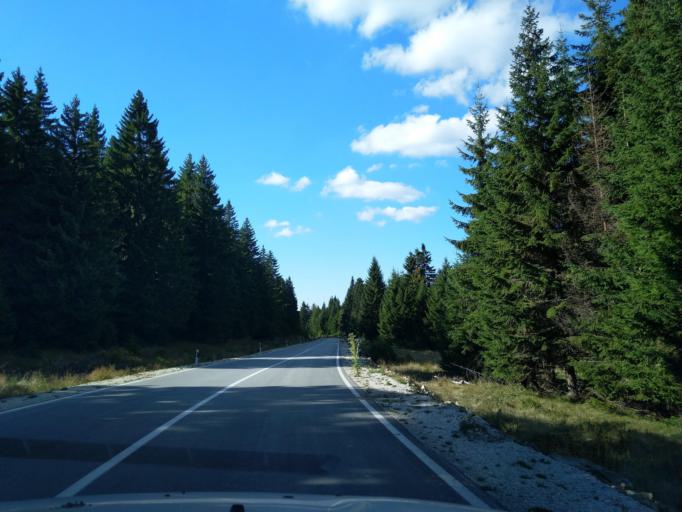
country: RS
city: Sokolovica
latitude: 43.2832
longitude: 20.3260
